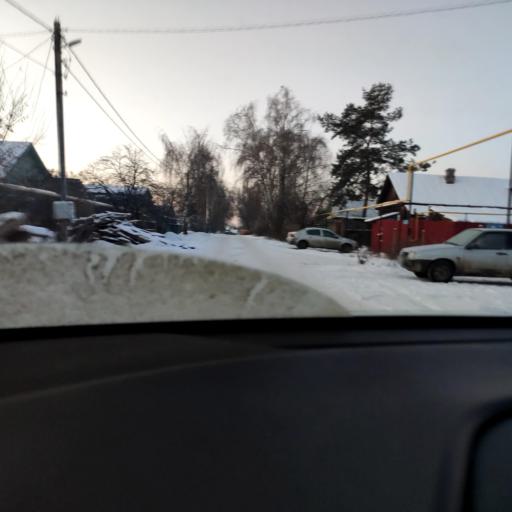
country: RU
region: Tatarstan
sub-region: Gorod Kazan'
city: Kazan
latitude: 55.7425
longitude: 49.0989
